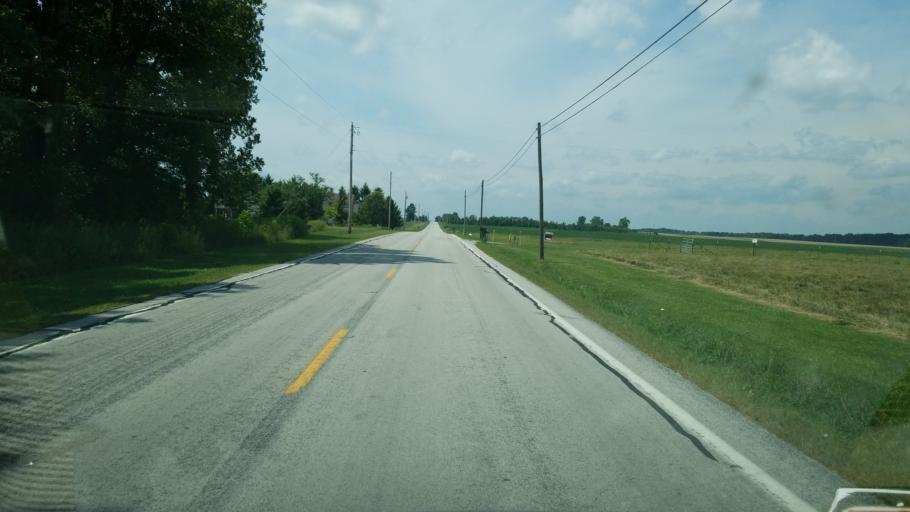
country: US
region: Ohio
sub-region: Hancock County
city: Arlington
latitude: 40.8915
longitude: -83.5874
